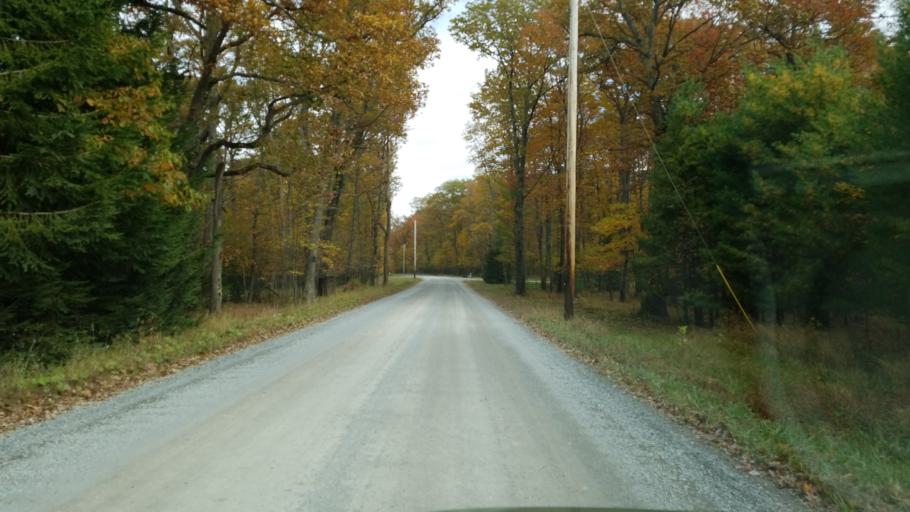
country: US
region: Pennsylvania
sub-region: Clearfield County
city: Clearfield
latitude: 41.1606
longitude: -78.4532
